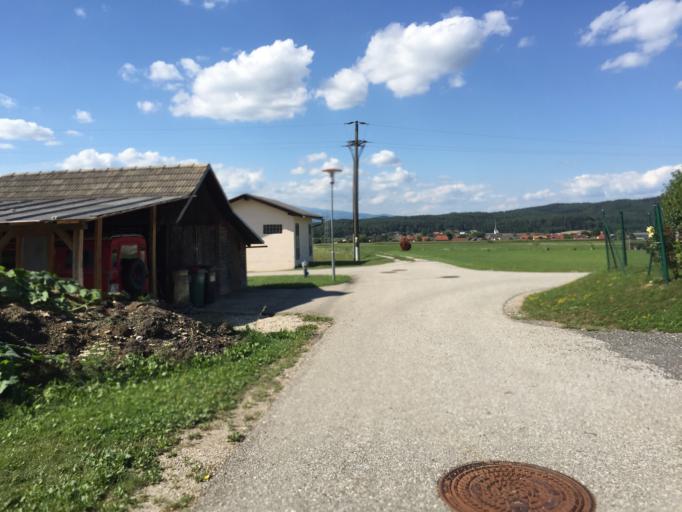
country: AT
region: Carinthia
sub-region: Politischer Bezirk Volkermarkt
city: Feistritz ob Bleiburg
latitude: 46.5631
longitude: 14.7629
